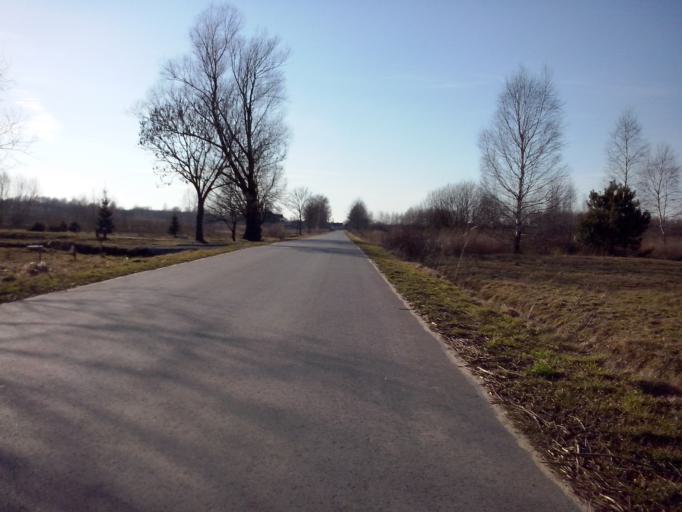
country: PL
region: Subcarpathian Voivodeship
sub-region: Powiat nizanski
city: Krzeszow
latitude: 50.4106
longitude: 22.3637
